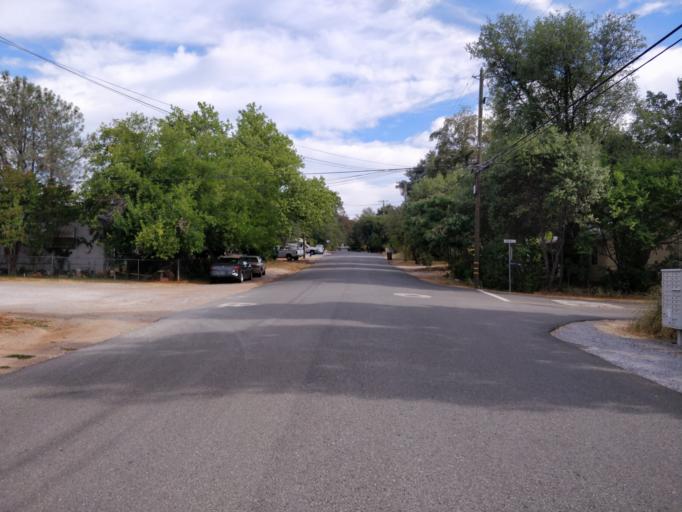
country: US
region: California
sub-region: Shasta County
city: Shasta Lake
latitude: 40.6828
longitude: -122.3568
